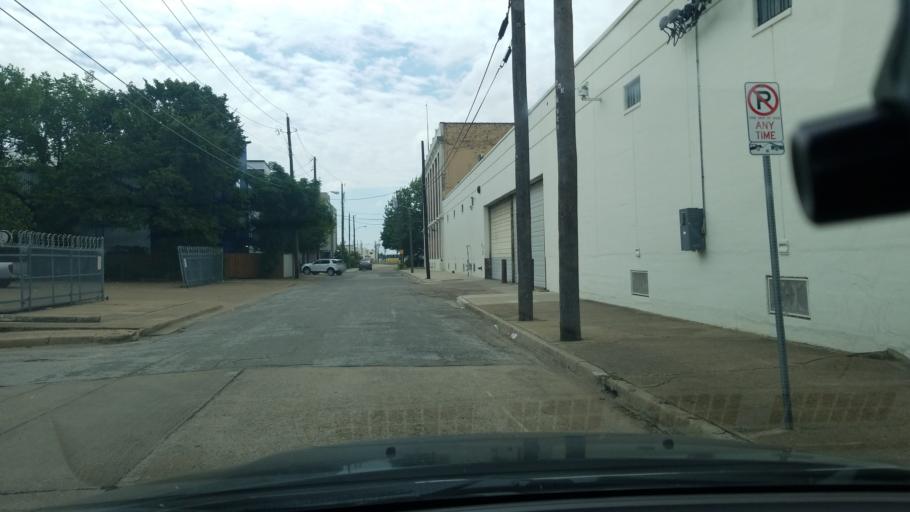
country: US
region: Texas
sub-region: Dallas County
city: Dallas
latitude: 32.7687
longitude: -96.7926
